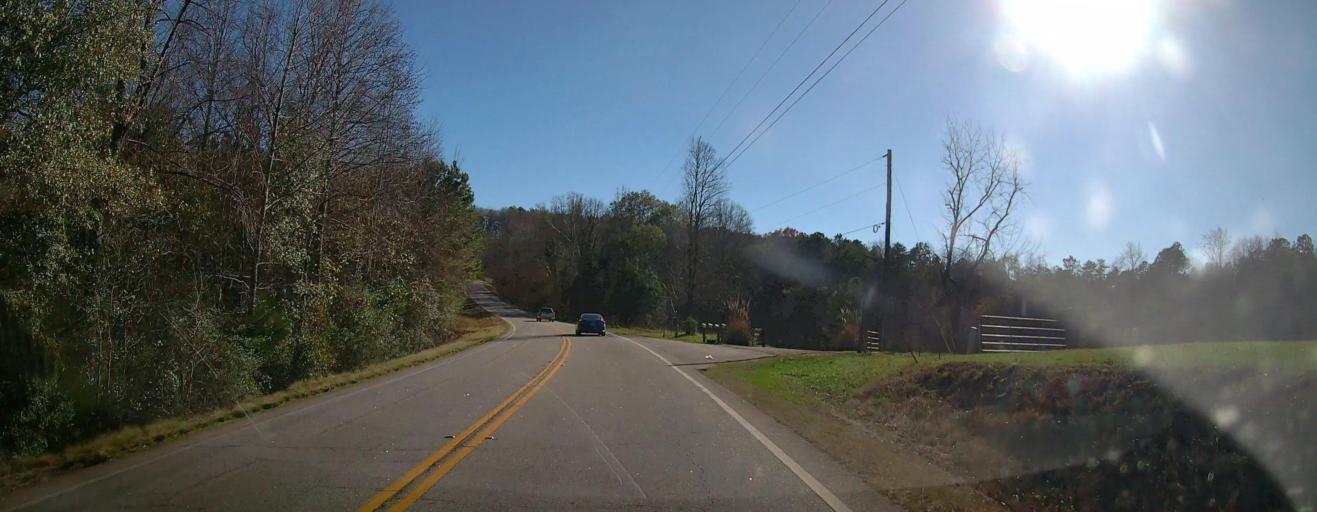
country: US
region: Georgia
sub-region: Hall County
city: Lula
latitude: 34.4101
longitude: -83.7101
